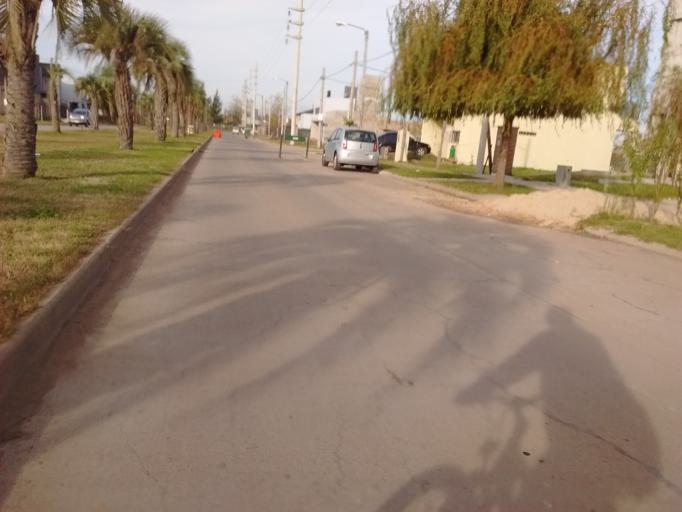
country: AR
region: Santa Fe
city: Roldan
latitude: -32.9326
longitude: -60.8918
